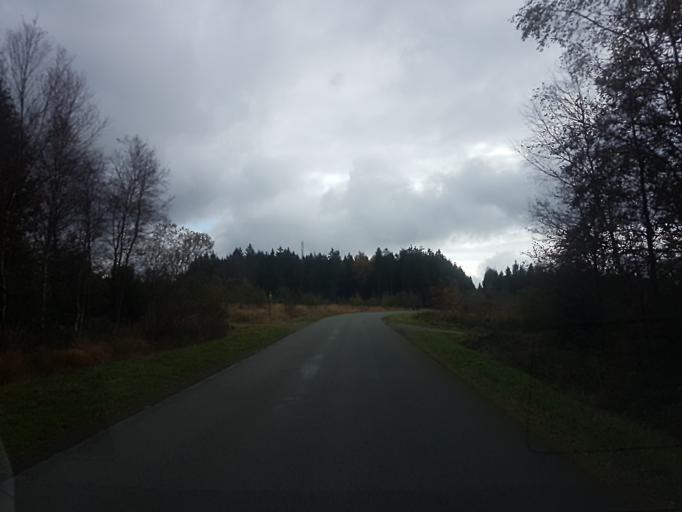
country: BE
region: Wallonia
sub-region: Province de Liege
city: Malmedy
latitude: 50.4765
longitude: 6.0179
